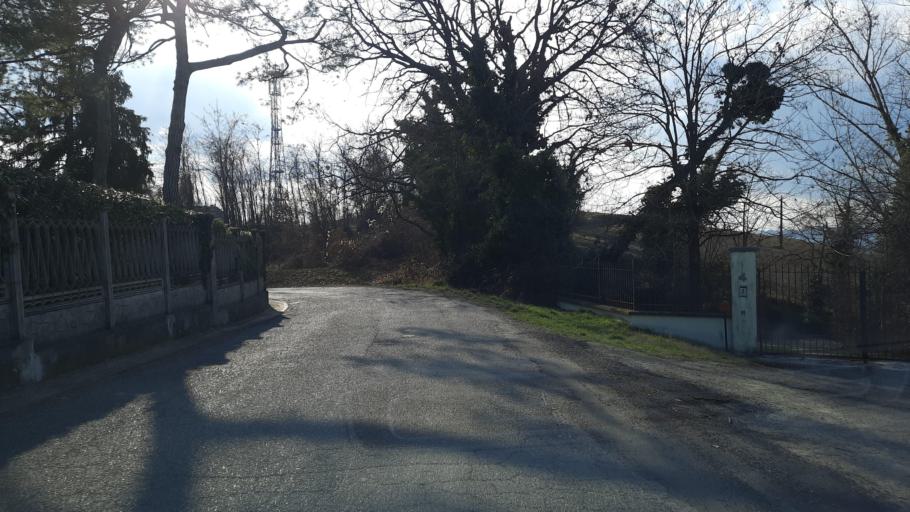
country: IT
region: Piedmont
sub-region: Provincia di Alessandria
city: Ozzano Monferrato
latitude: 45.1162
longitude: 8.3834
